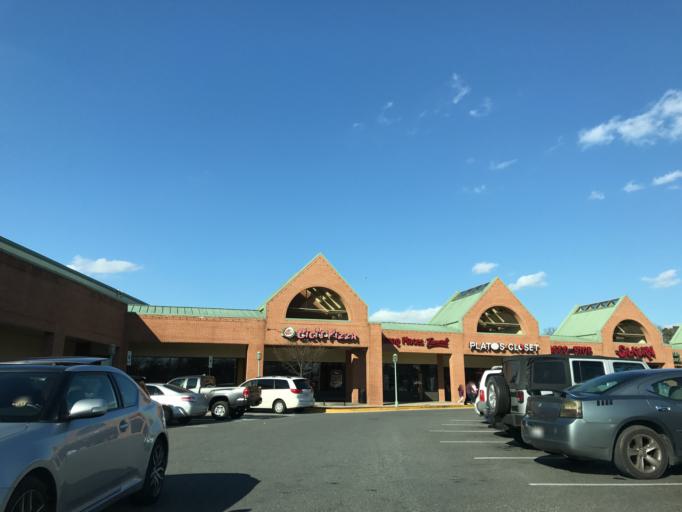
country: US
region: Maryland
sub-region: Anne Arundel County
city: South Gate
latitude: 39.1366
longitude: -76.5955
